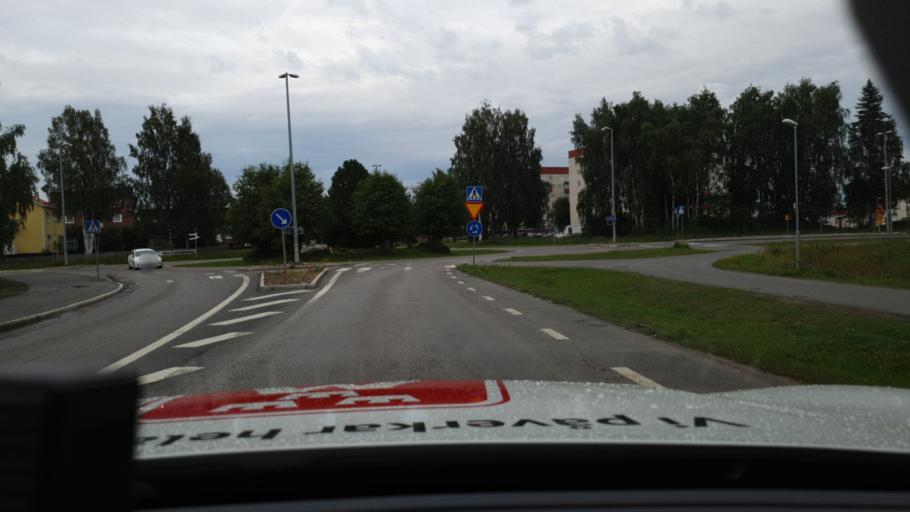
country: SE
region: Norrbotten
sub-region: Bodens Kommun
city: Boden
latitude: 65.8237
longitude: 21.6671
